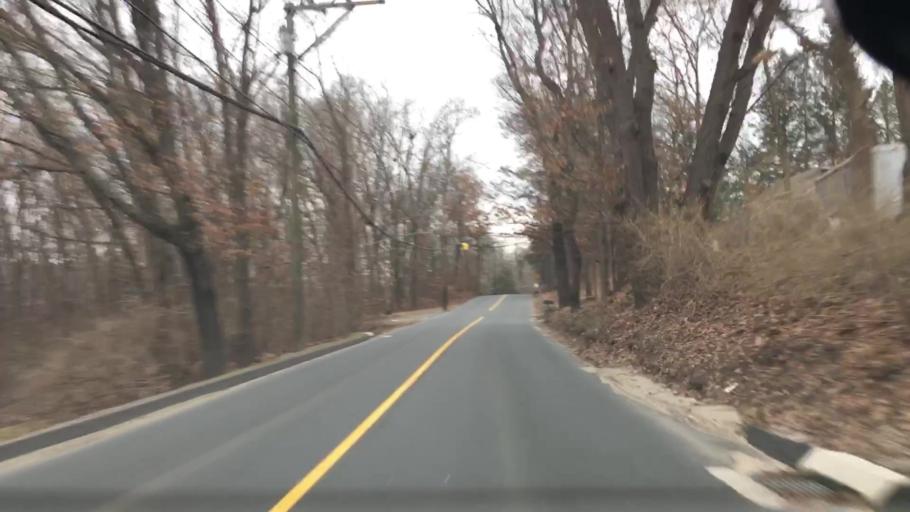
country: US
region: Connecticut
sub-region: Fairfield County
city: Bethel
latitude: 41.3937
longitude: -73.4002
